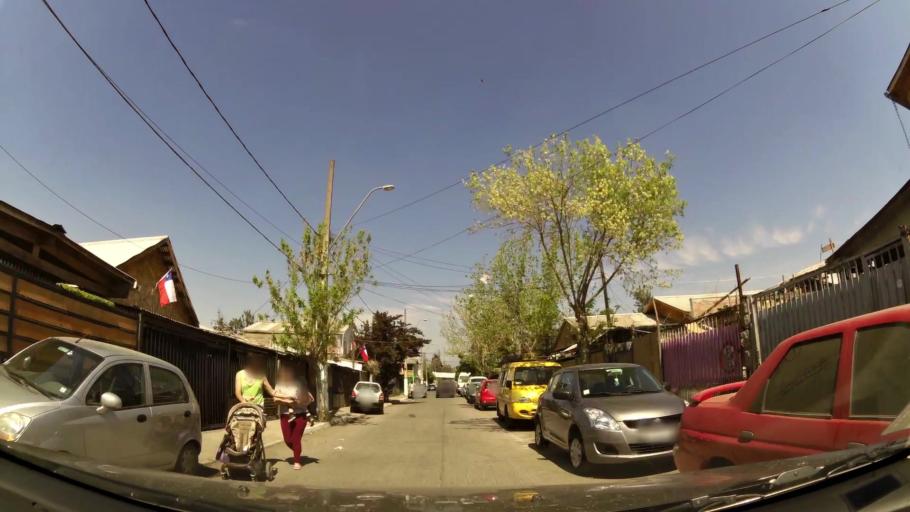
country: CL
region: Santiago Metropolitan
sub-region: Provincia de Santiago
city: La Pintana
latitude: -33.5929
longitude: -70.6255
